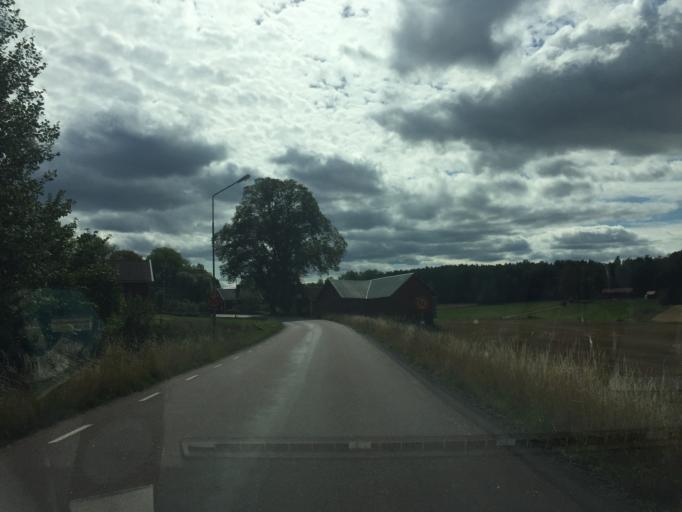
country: SE
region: OErebro
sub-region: Askersunds Kommun
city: Asbro
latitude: 59.0738
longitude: 15.0060
